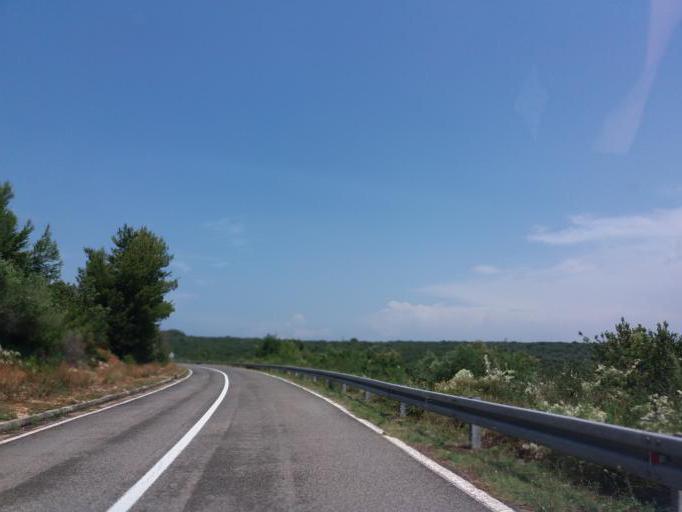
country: HR
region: Zadarska
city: Sali
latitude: 43.9723
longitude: 15.1099
